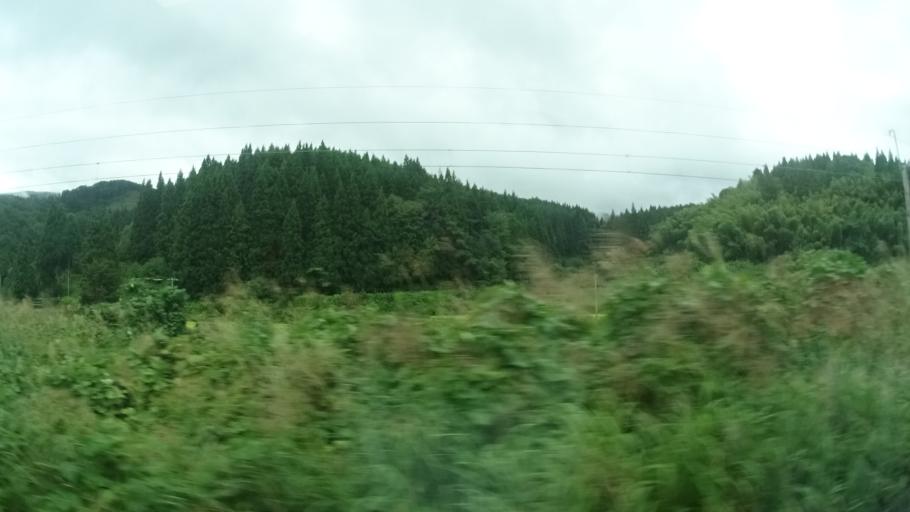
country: JP
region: Yamagata
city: Tsuruoka
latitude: 38.7023
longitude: 139.7074
